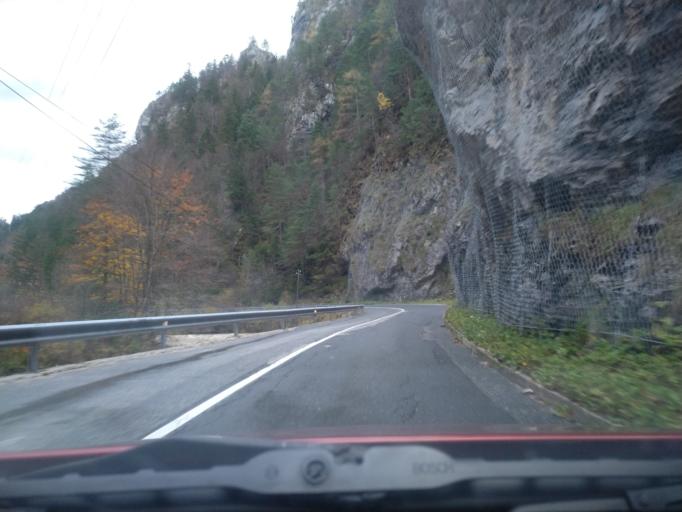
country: SI
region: Luce
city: Luce
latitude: 46.3809
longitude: 14.7272
